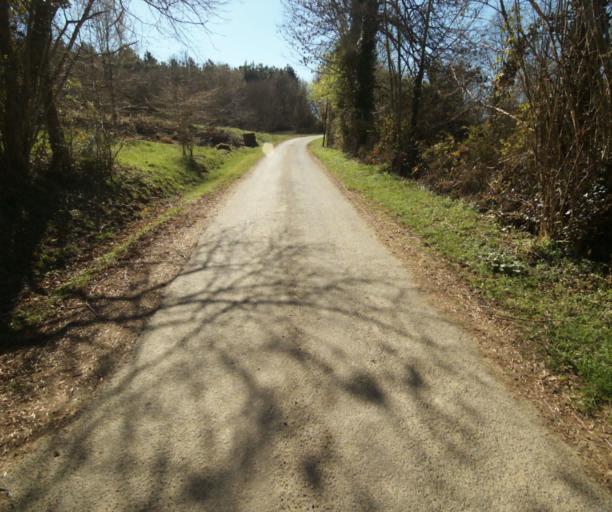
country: FR
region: Limousin
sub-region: Departement de la Correze
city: Chamboulive
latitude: 45.4084
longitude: 1.7295
